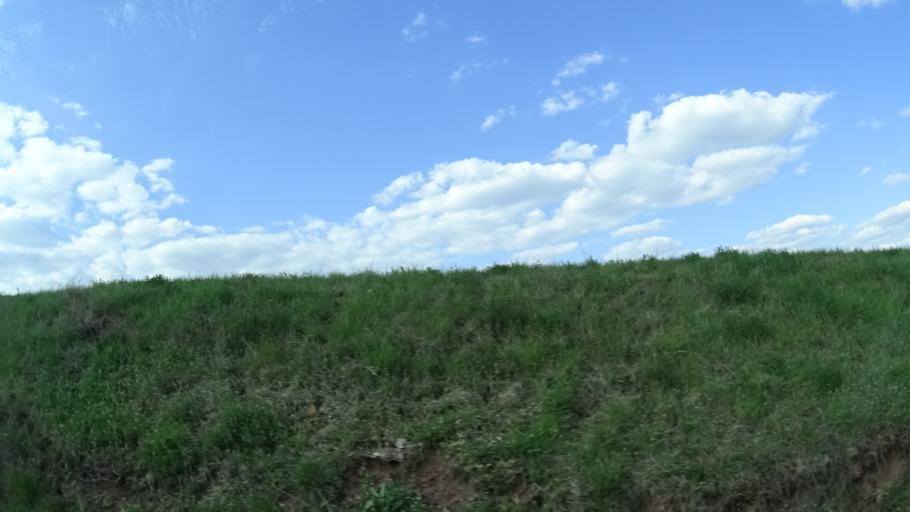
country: DE
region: Rheinland-Pfalz
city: Limbach
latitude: 49.7251
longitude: 7.5495
